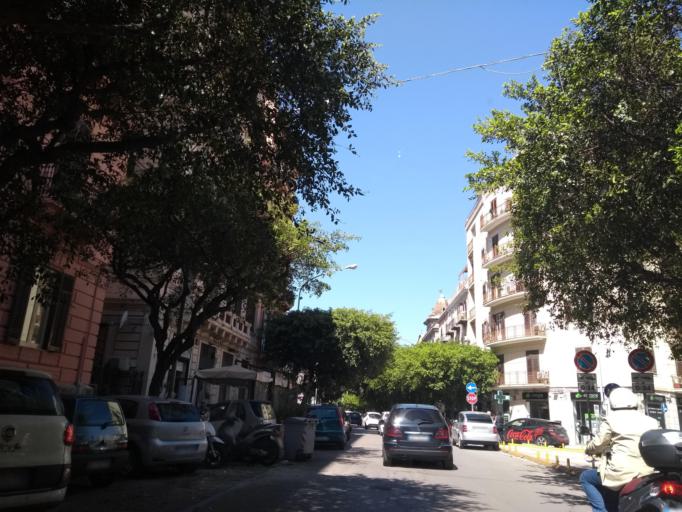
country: IT
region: Sicily
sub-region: Palermo
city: Palermo
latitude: 38.1213
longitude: 13.3542
